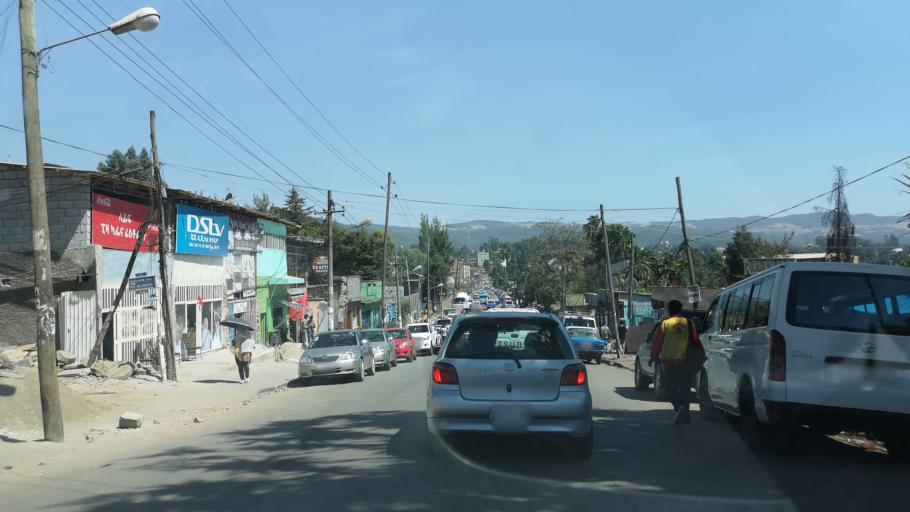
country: ET
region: Adis Abeba
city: Addis Ababa
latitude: 9.0486
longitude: 38.7467
